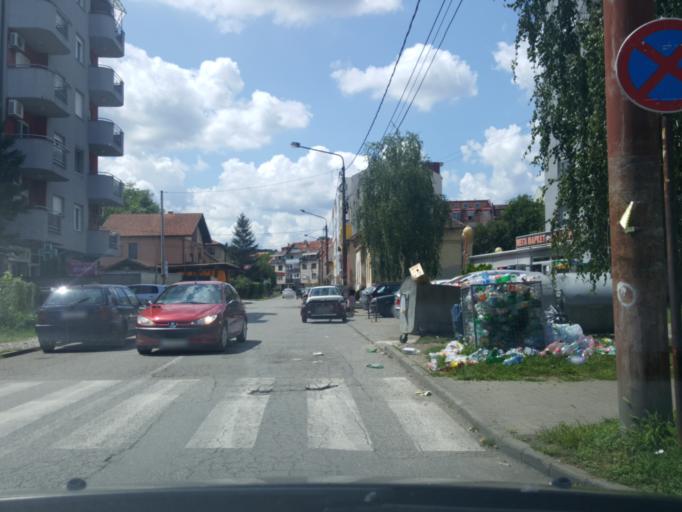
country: RS
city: Trsic
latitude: 44.5285
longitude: 19.2243
